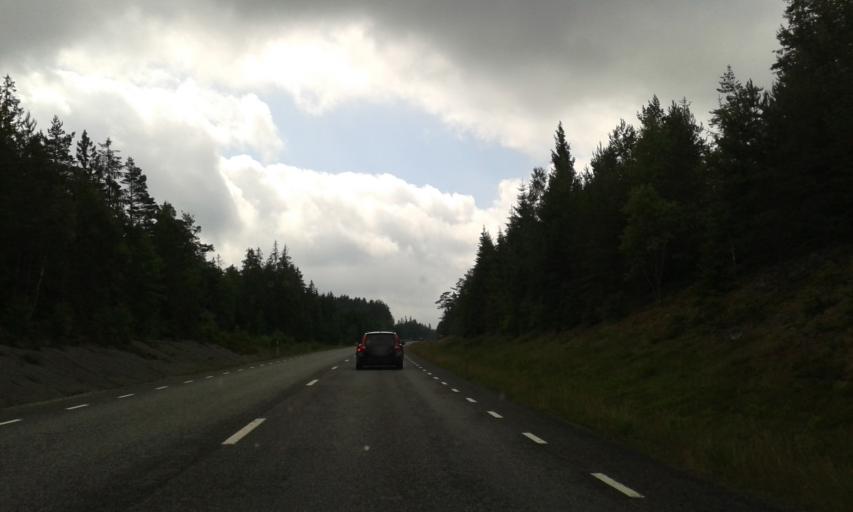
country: SE
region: Vaestra Goetaland
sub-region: Tranemo Kommun
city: Tranemo
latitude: 57.4227
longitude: 13.4505
